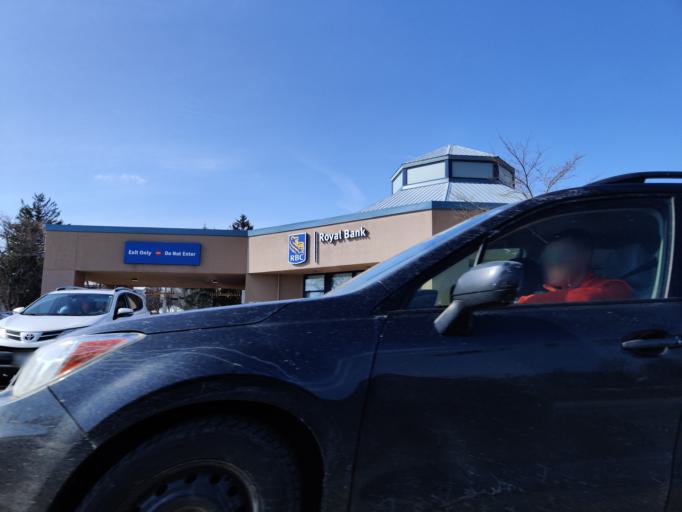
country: CA
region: Ontario
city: Collingwood
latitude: 44.4961
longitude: -80.2161
